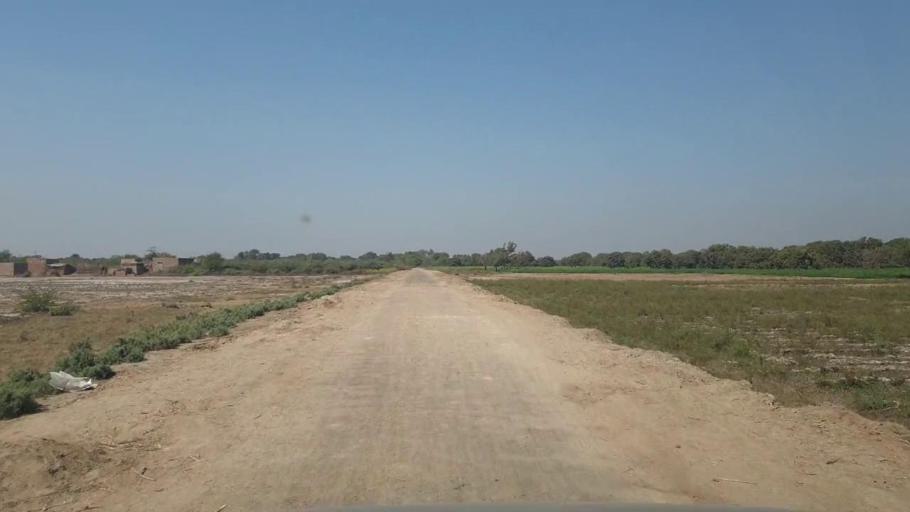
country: PK
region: Sindh
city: Digri
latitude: 25.2495
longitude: 69.2335
